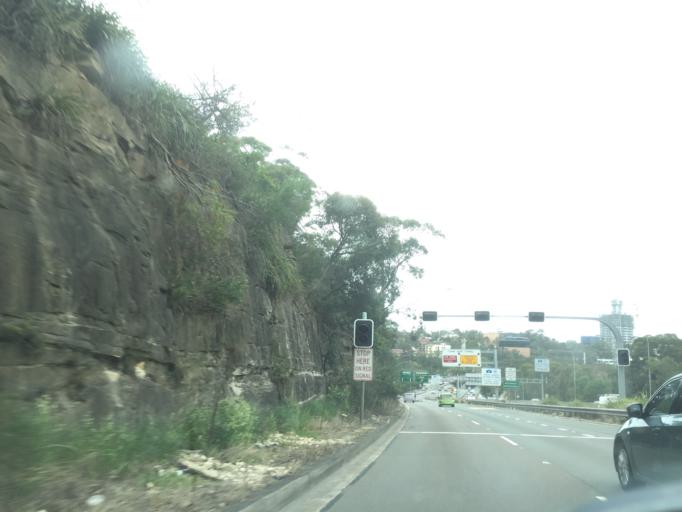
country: AU
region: New South Wales
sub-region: Ryde
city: East Ryde
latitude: -33.7989
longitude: 151.1405
